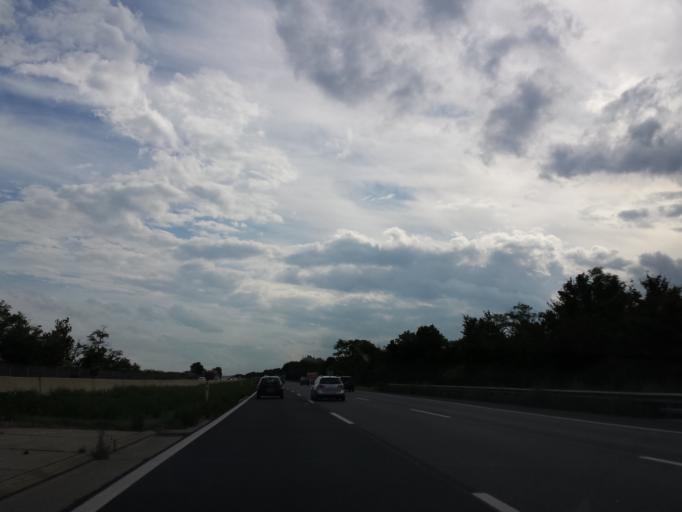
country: AT
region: Lower Austria
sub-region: Politischer Bezirk Baden
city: Kottingbrunn
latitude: 47.9460
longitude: 16.2150
